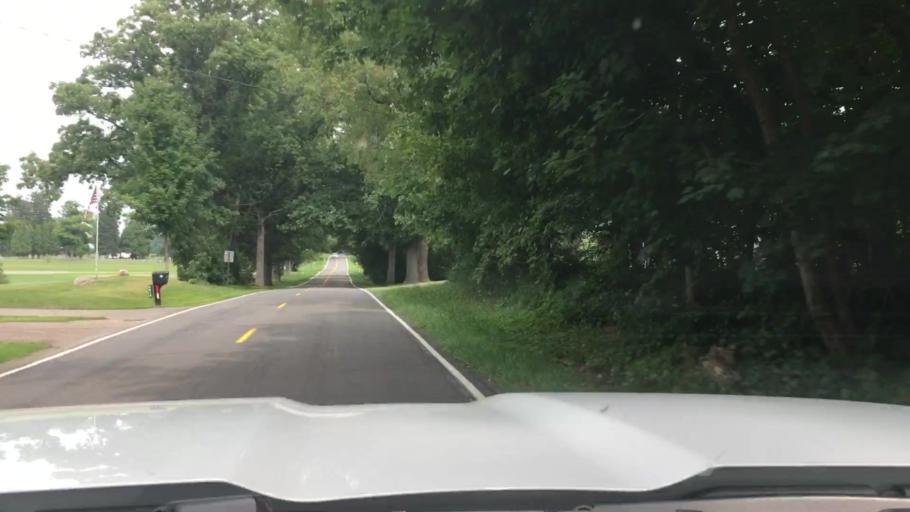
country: US
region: Michigan
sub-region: Ingham County
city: Webberville
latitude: 42.6697
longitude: -84.1888
